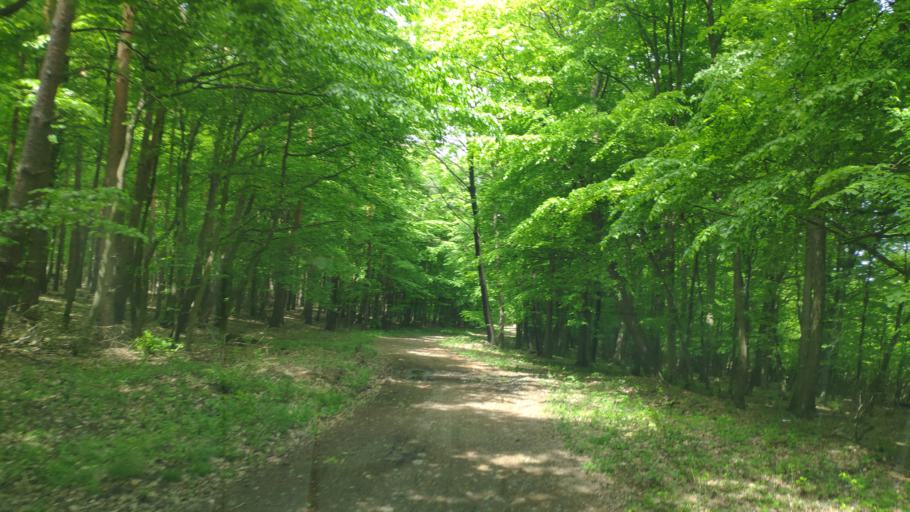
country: SK
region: Kosicky
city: Secovce
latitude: 48.7056
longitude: 21.5854
